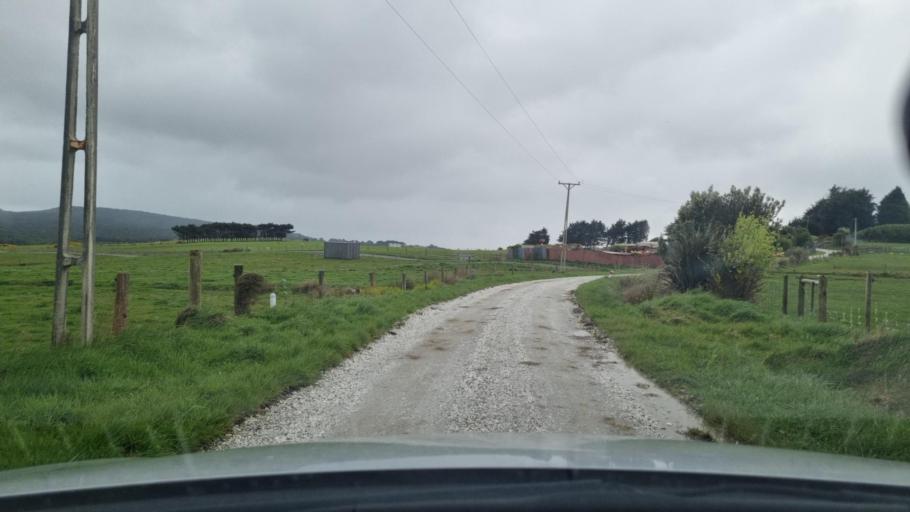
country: NZ
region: Southland
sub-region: Invercargill City
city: Bluff
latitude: -46.5406
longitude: 168.2908
